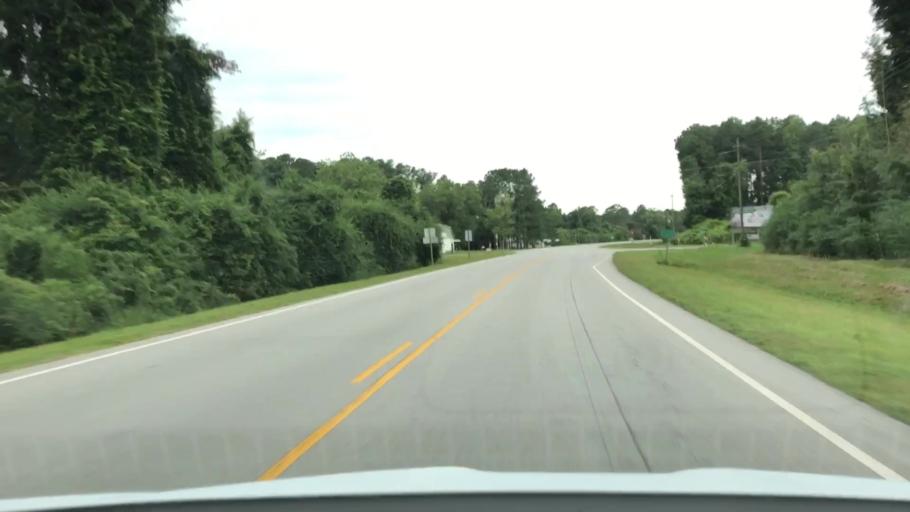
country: US
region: North Carolina
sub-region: Jones County
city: Trenton
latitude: 35.0181
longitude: -77.3005
